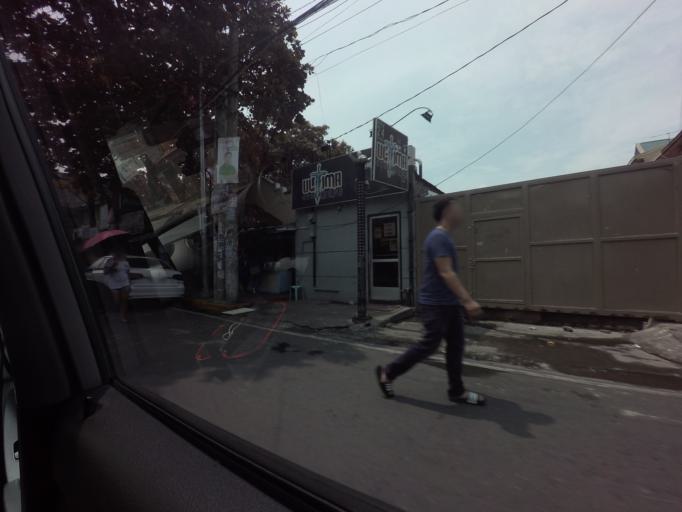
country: PH
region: Metro Manila
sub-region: City of Manila
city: Port Area
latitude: 14.5711
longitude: 120.9942
